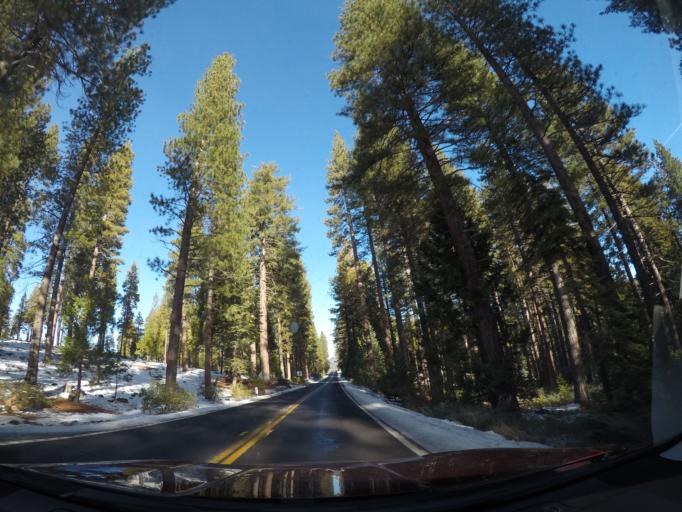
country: US
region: California
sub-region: Tuolumne County
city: Twain Harte
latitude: 38.1803
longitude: -120.0179
